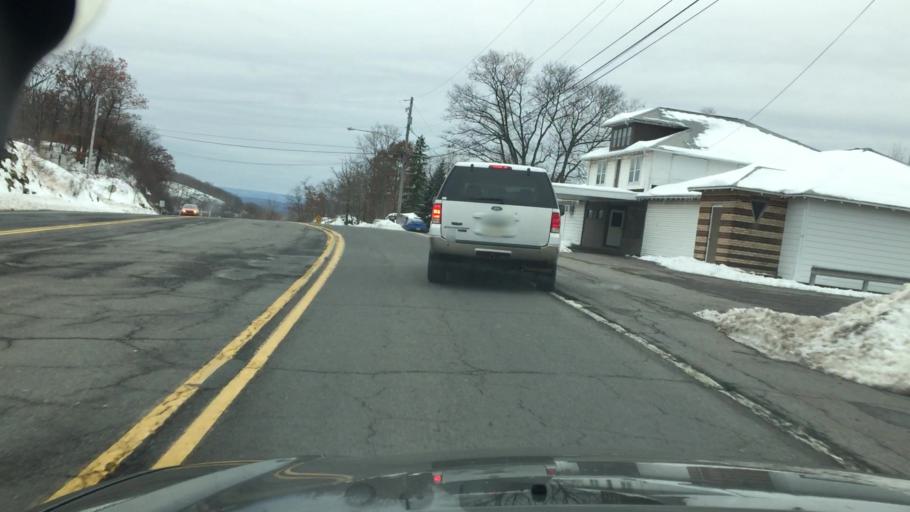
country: US
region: Pennsylvania
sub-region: Luzerne County
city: Mountain Top
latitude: 41.1777
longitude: -75.8825
